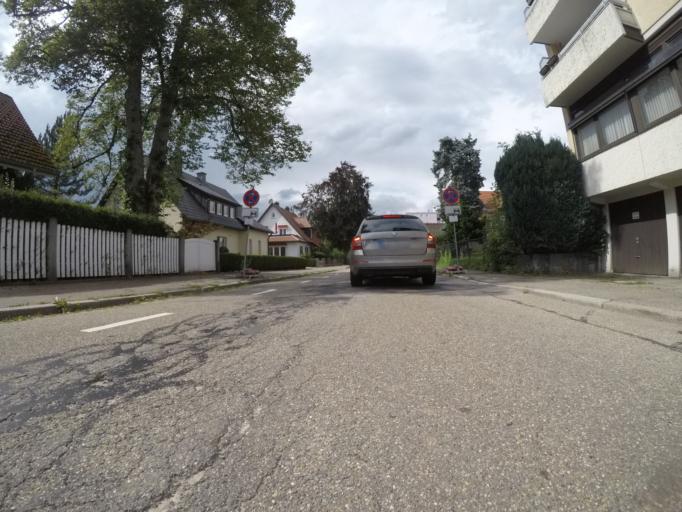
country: DE
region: Baden-Wuerttemberg
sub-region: Karlsruhe Region
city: Freudenstadt
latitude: 48.4625
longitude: 8.4090
